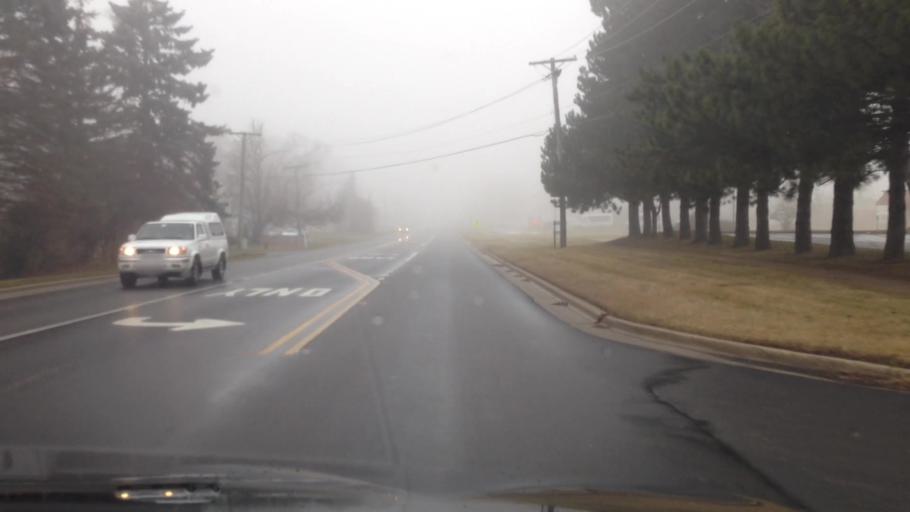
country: US
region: Illinois
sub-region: McHenry County
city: Woodstock
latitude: 42.3365
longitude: -88.4432
